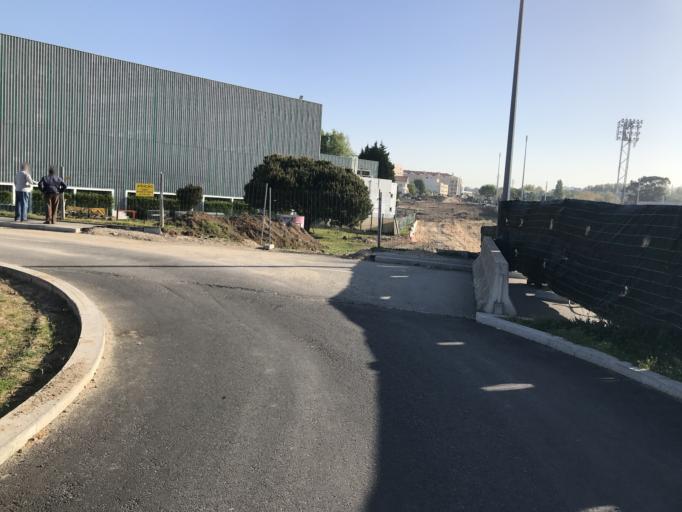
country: PT
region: Porto
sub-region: Matosinhos
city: Guifoes
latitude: 41.1840
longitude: -8.6684
